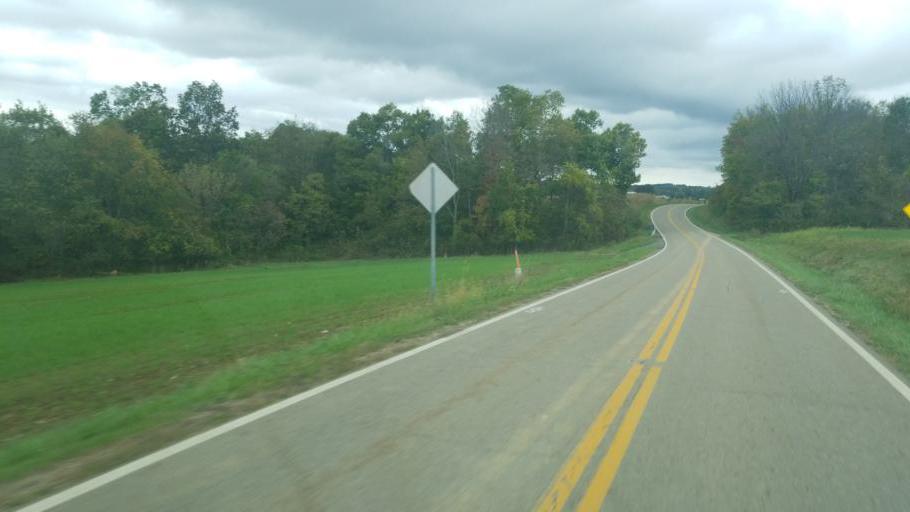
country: US
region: Ohio
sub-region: Ashland County
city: Loudonville
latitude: 40.5356
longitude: -82.1565
